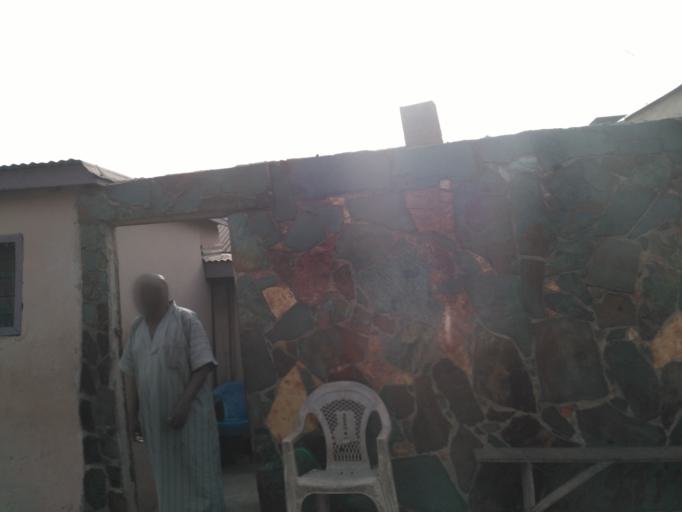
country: GH
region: Ashanti
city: Kumasi
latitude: 6.6992
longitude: -1.6056
